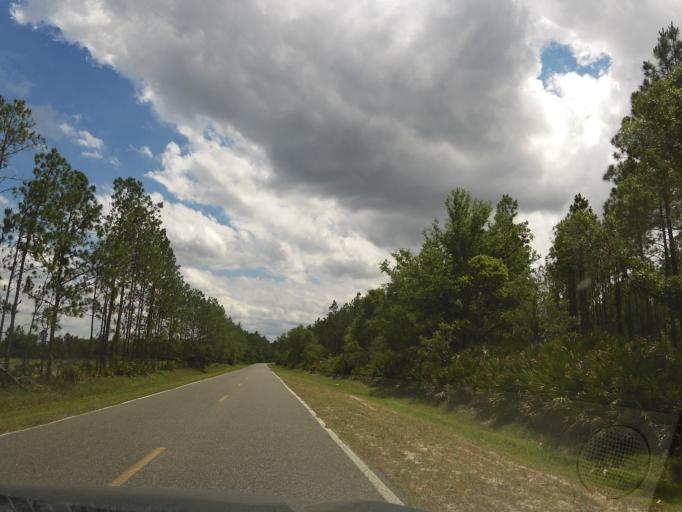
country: US
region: Florida
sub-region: Clay County
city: Green Cove Springs
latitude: 29.9247
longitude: -81.7571
